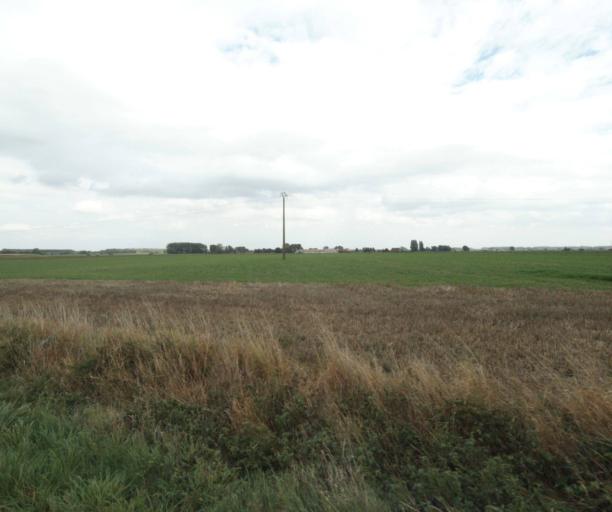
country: FR
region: Nord-Pas-de-Calais
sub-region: Departement du Nord
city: Illies
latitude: 50.5479
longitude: 2.8381
